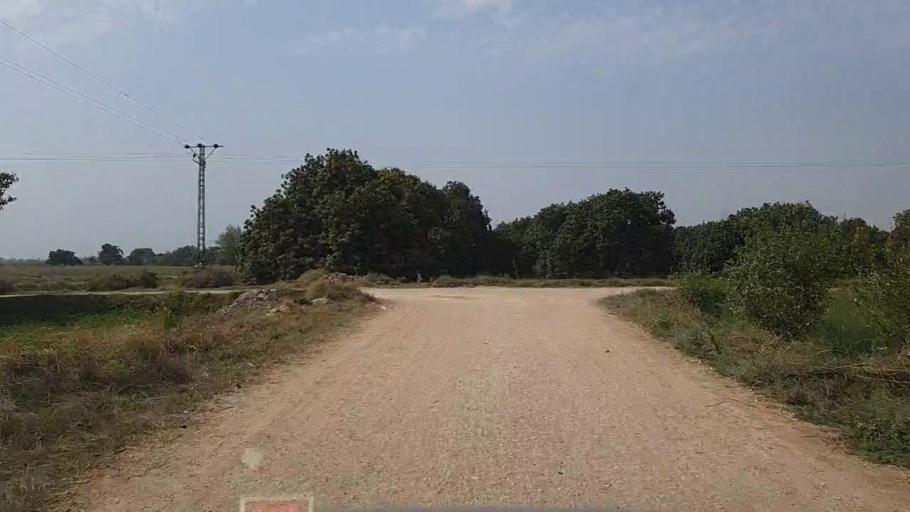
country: PK
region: Sindh
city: Mirwah Gorchani
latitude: 25.3503
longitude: 69.0541
